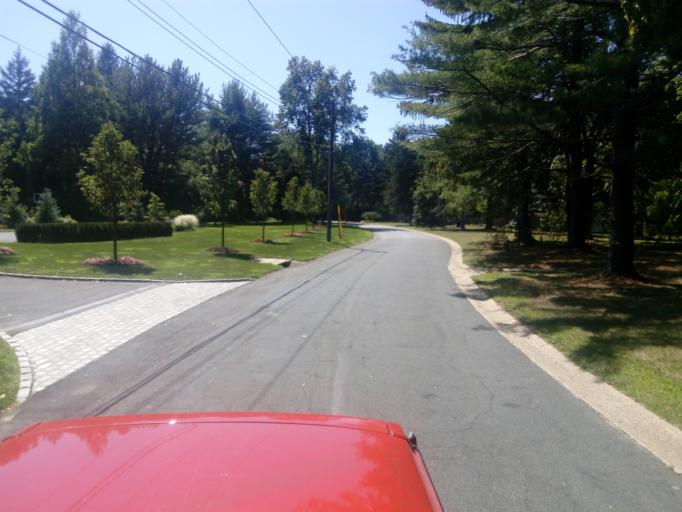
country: US
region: New York
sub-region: Nassau County
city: Upper Brookville
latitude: 40.8428
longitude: -73.5783
